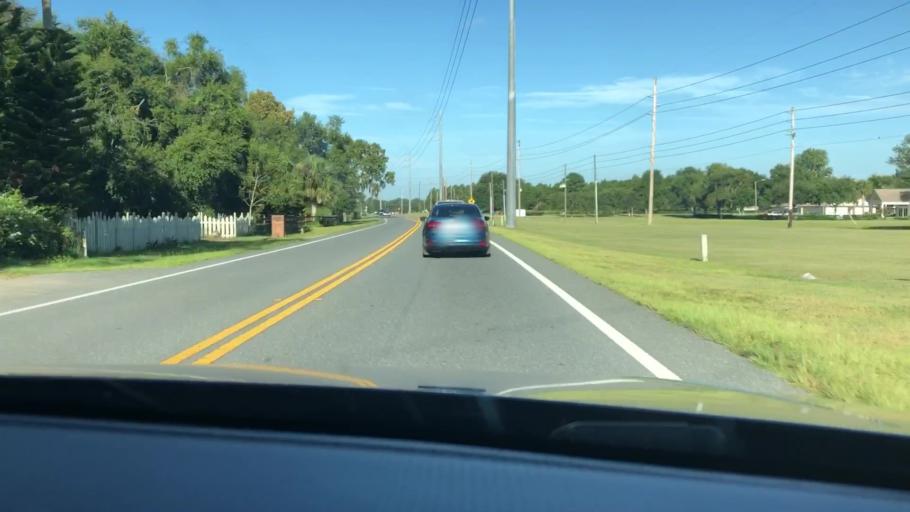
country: US
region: Florida
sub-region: Lake County
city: Eustis
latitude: 28.8824
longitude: -81.7344
